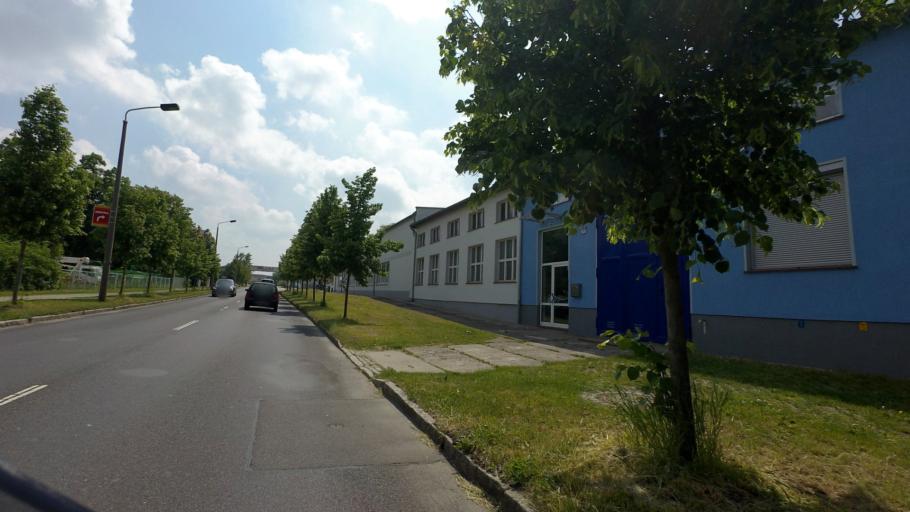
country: DE
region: Brandenburg
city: Spremberg
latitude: 51.5741
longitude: 14.3649
